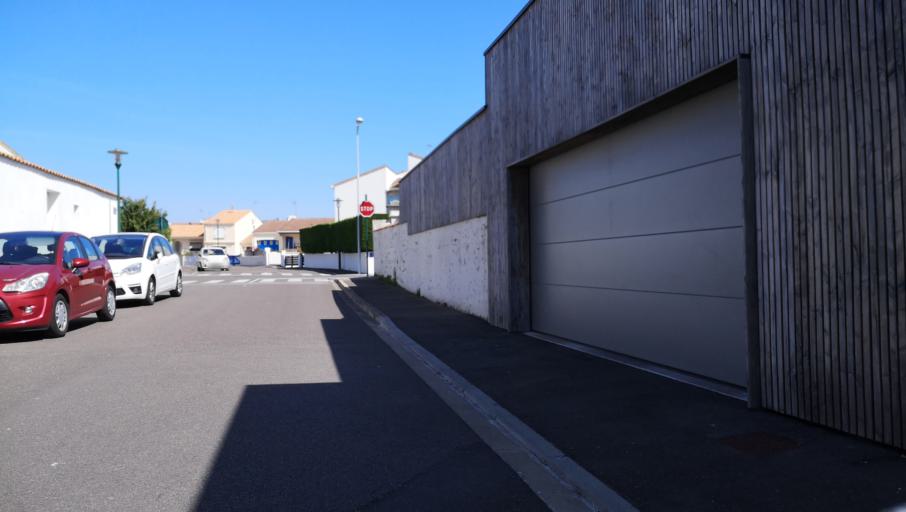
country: FR
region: Pays de la Loire
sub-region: Departement de la Vendee
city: Les Sables-d'Olonne
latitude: 46.4967
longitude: -1.7662
